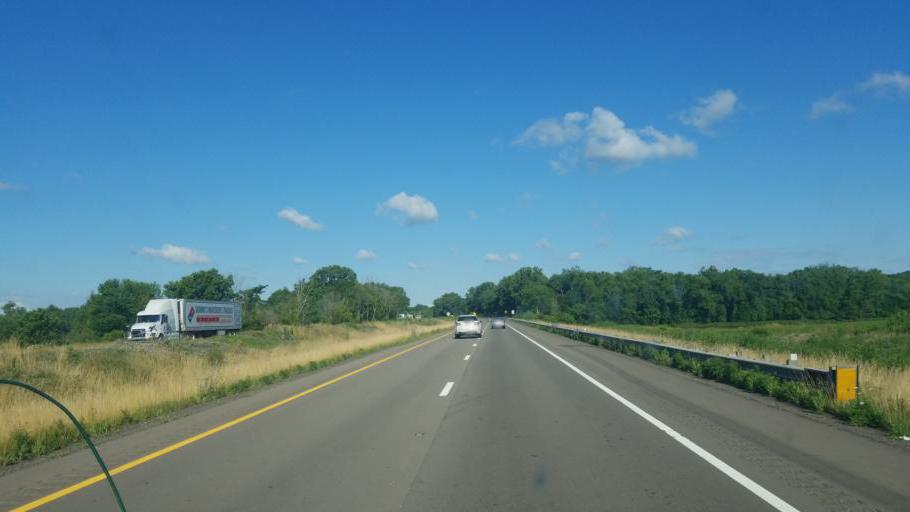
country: US
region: Ohio
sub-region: Ashland County
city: Loudonville
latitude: 40.7844
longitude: -82.1577
